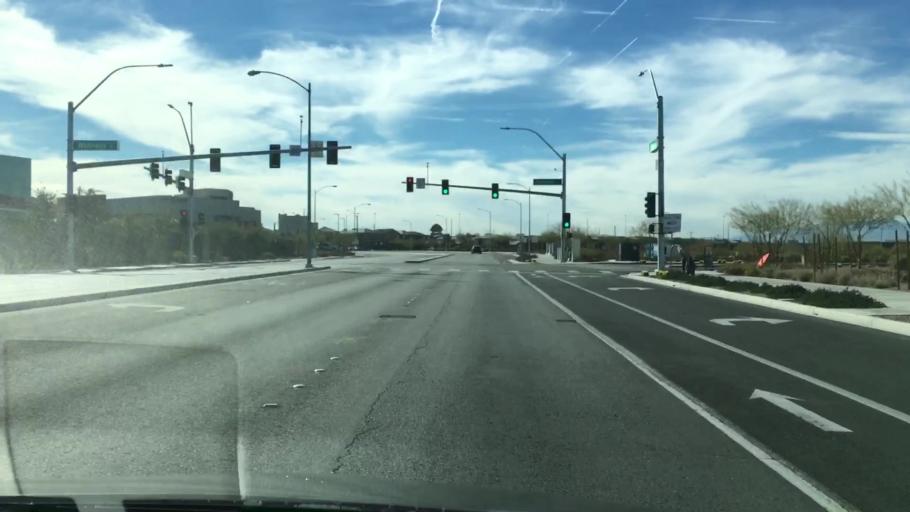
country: US
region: Nevada
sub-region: Clark County
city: Henderson
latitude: 36.0732
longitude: -115.0265
